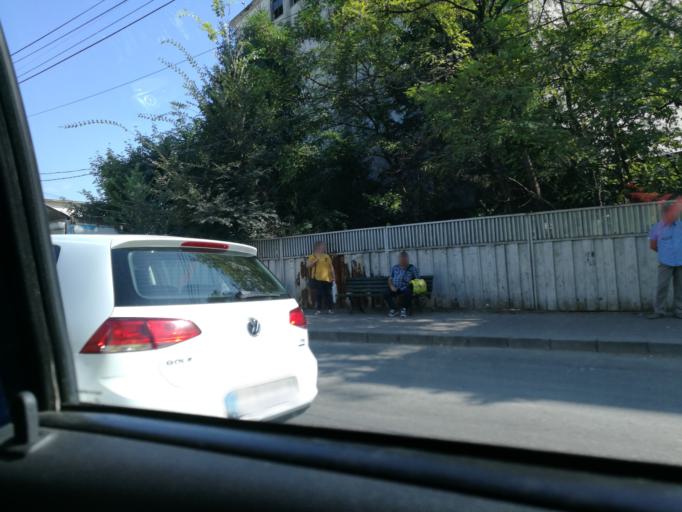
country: RO
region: Iasi
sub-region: Comuna Miroslava
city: Miroslava
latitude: 47.1735
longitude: 27.5501
